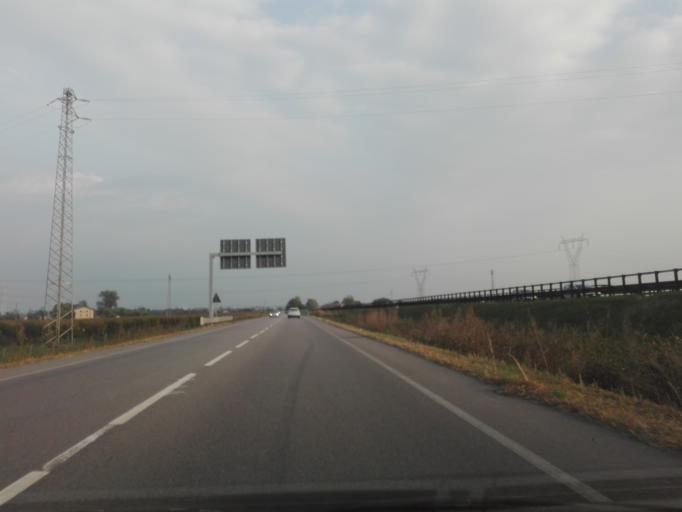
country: IT
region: Veneto
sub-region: Provincia di Verona
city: Bussolengo
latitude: 45.4628
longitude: 10.8314
